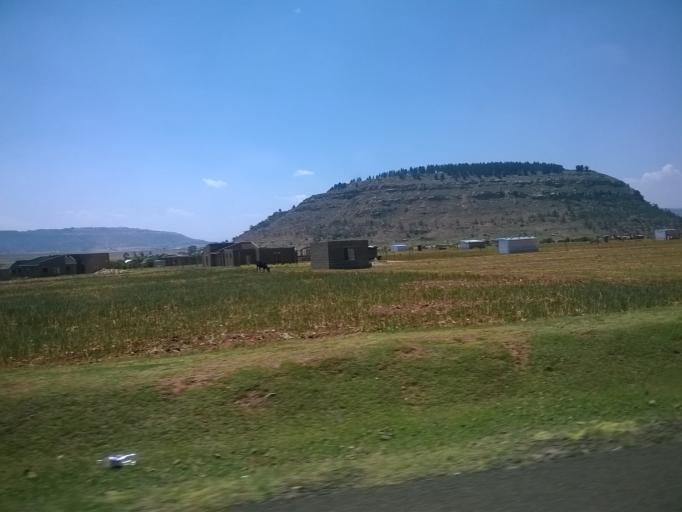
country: LS
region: Leribe
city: Maputsoe
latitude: -28.9508
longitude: 27.9603
